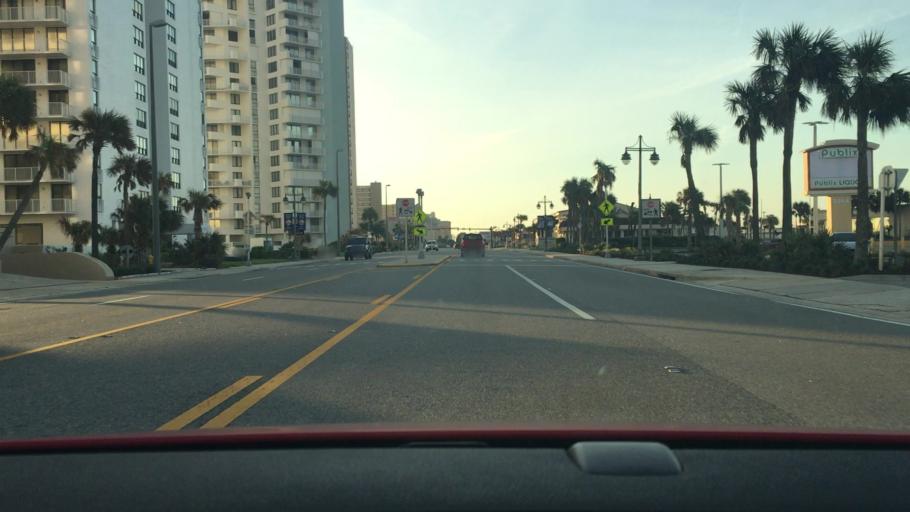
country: US
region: Florida
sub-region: Volusia County
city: Daytona Beach Shores
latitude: 29.1680
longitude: -80.9782
